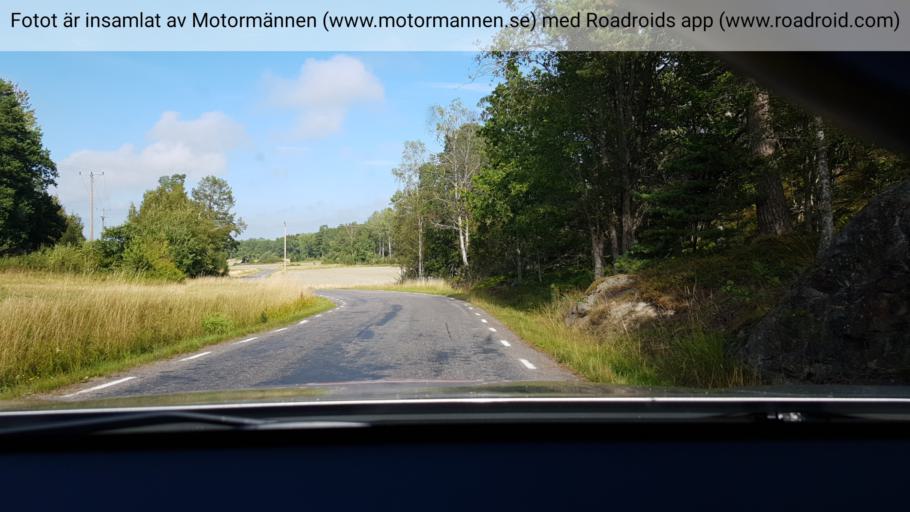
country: SE
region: Stockholm
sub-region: Nynashamns Kommun
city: Osmo
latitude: 58.8867
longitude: 17.7900
